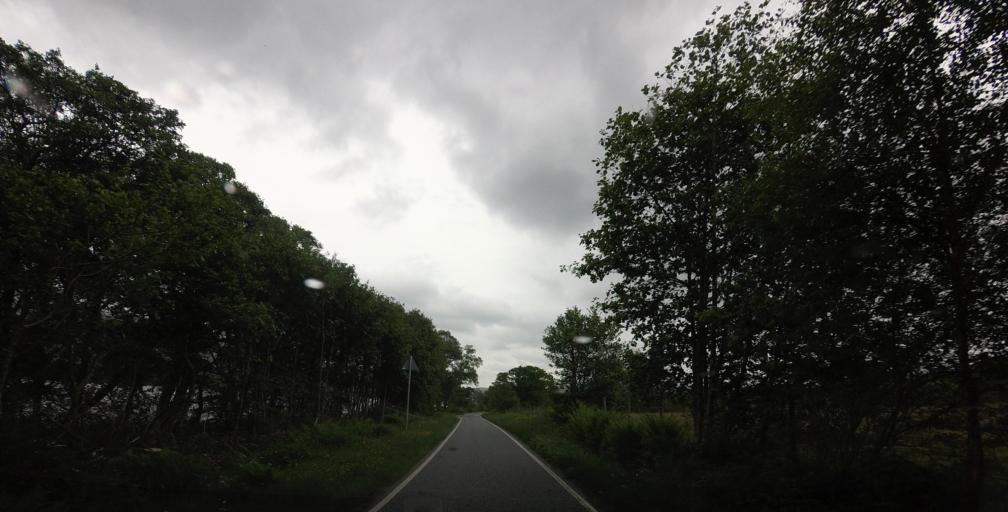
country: GB
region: Scotland
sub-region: Highland
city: Fort William
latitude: 56.8422
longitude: -5.2420
